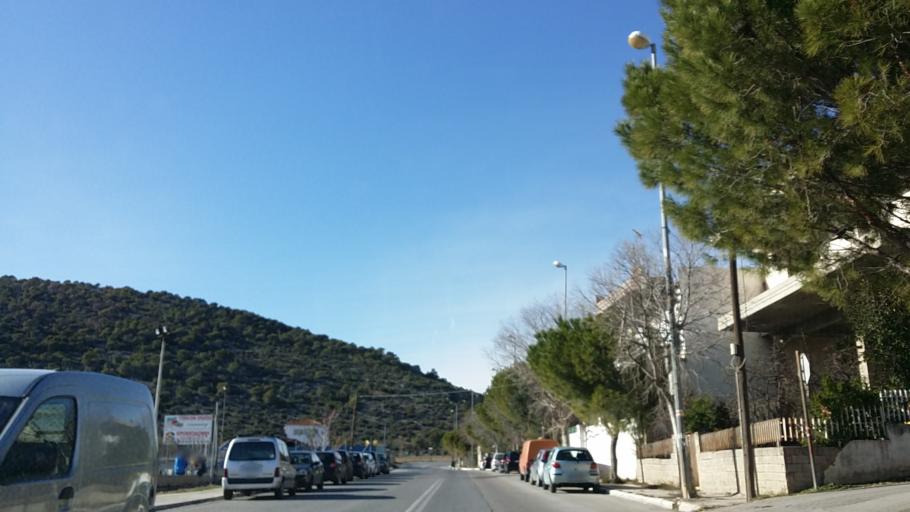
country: GR
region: Attica
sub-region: Nomarchia Dytikis Attikis
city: Fyli
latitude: 38.0969
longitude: 23.6848
